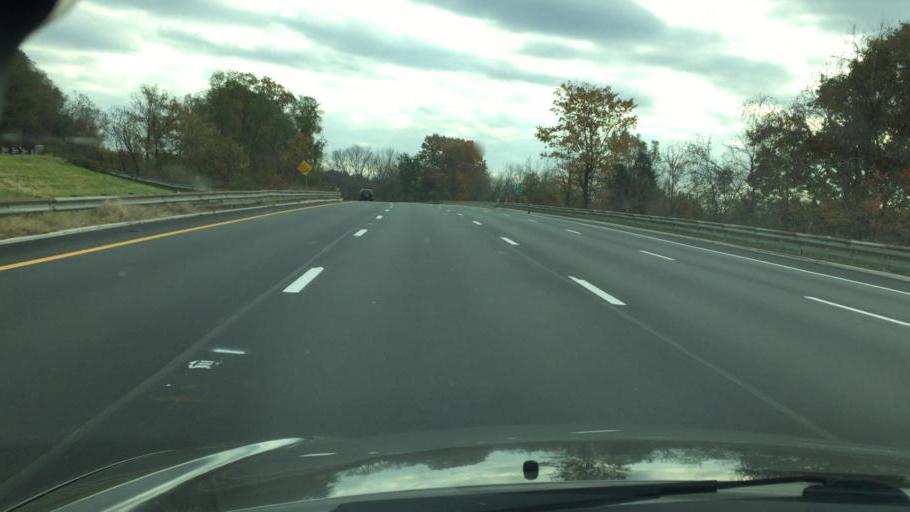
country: US
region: New Jersey
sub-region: Warren County
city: Belvidere
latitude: 40.9257
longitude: -75.0682
